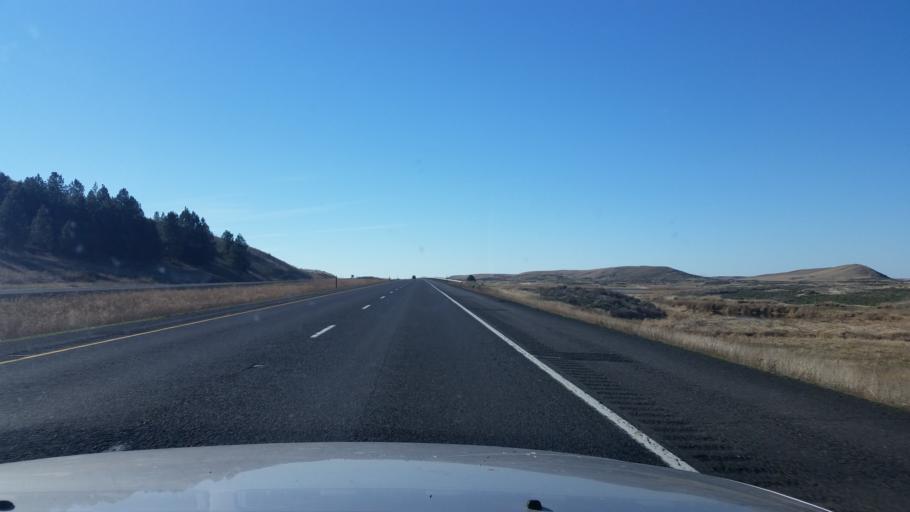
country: US
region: Washington
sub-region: Spokane County
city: Medical Lake
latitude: 47.3730
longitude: -117.8761
